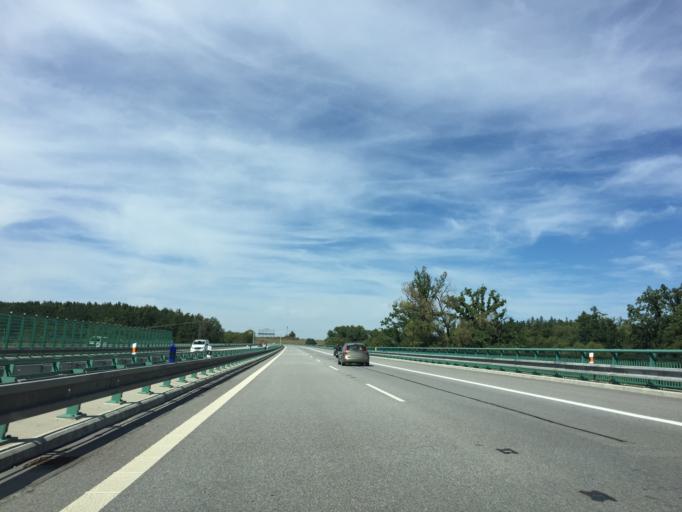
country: CZ
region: Jihocesky
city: Sobeslav
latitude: 49.2740
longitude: 14.7367
